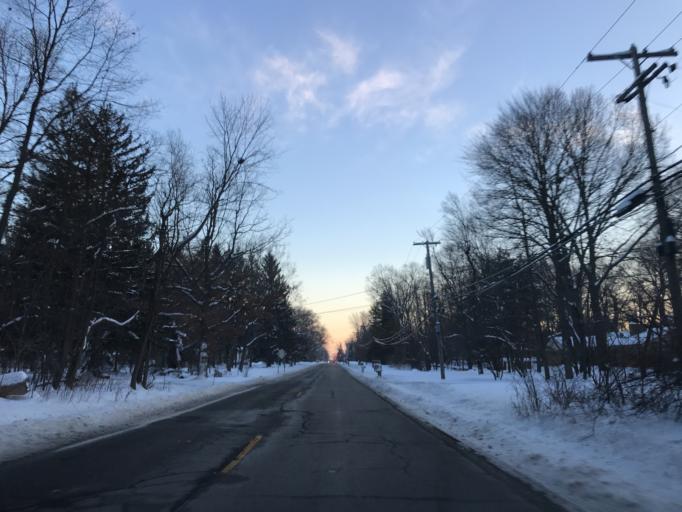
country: US
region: Michigan
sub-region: Oakland County
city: Bingham Farms
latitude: 42.4620
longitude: -83.2984
